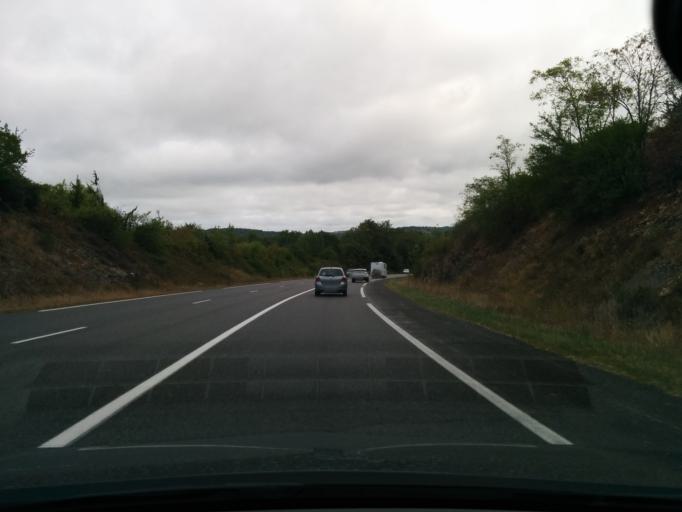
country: FR
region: Midi-Pyrenees
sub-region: Departement du Lot
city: Cahors
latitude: 44.4584
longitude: 1.4136
